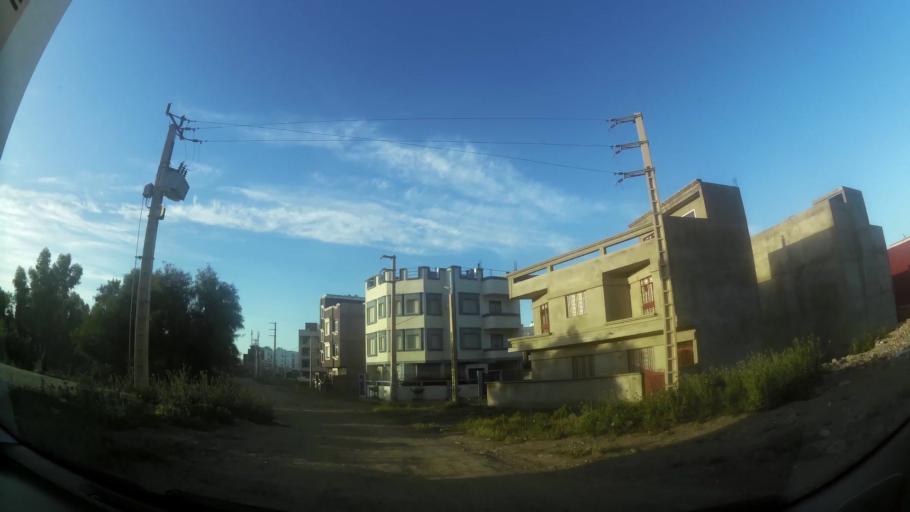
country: MA
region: Oriental
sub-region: Berkane-Taourirt
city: Madagh
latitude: 35.0767
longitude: -2.2350
